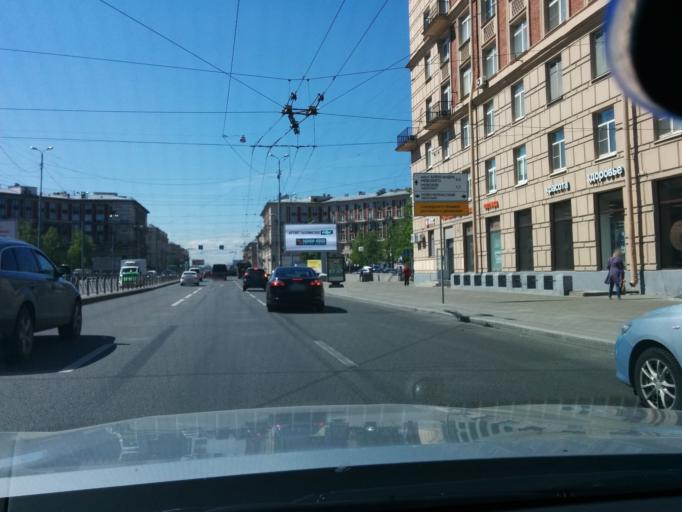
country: RU
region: St.-Petersburg
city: Centralniy
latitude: 59.9294
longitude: 30.4140
